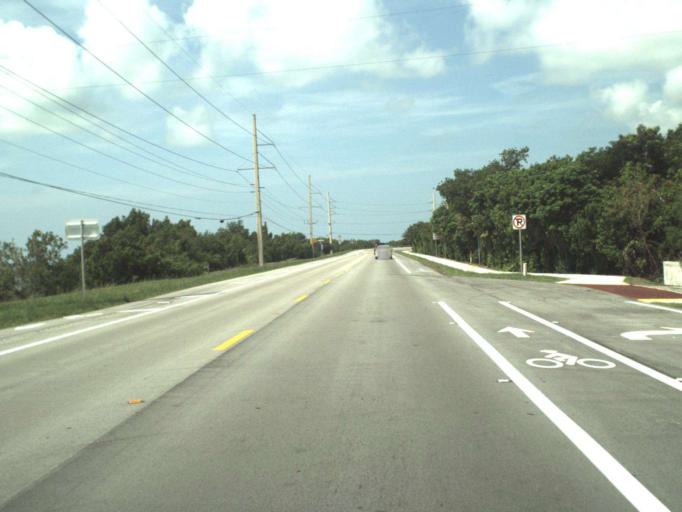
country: US
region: Florida
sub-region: Monroe County
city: Islamorada
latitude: 24.8383
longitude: -80.7590
